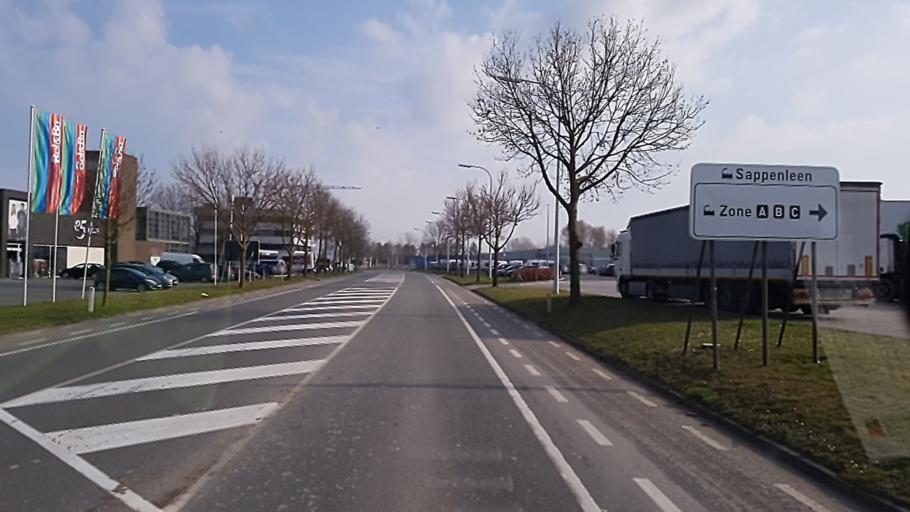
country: BE
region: Flanders
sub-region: Provincie West-Vlaanderen
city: Poperinge
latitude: 50.8510
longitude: 2.7429
